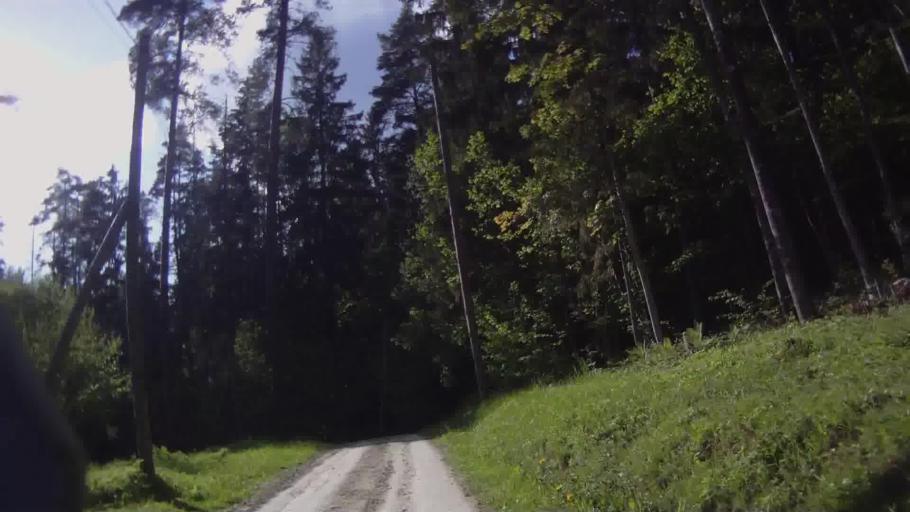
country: LV
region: Baldone
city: Baldone
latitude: 56.7498
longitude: 24.4183
